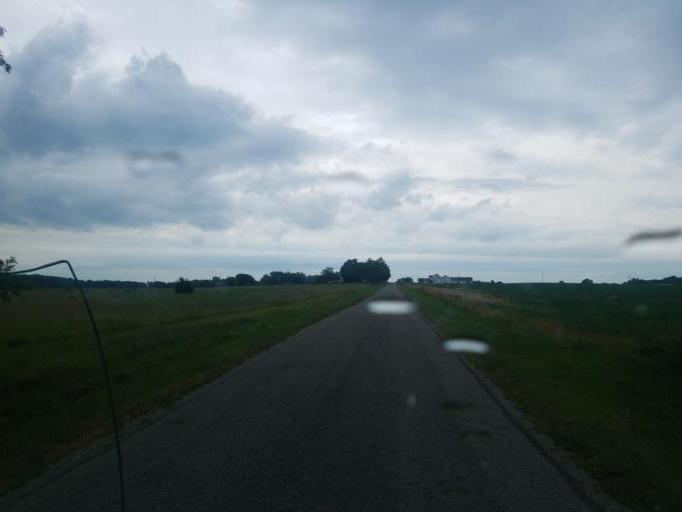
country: US
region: Ohio
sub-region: Defiance County
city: Hicksville
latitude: 41.3681
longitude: -84.7742
